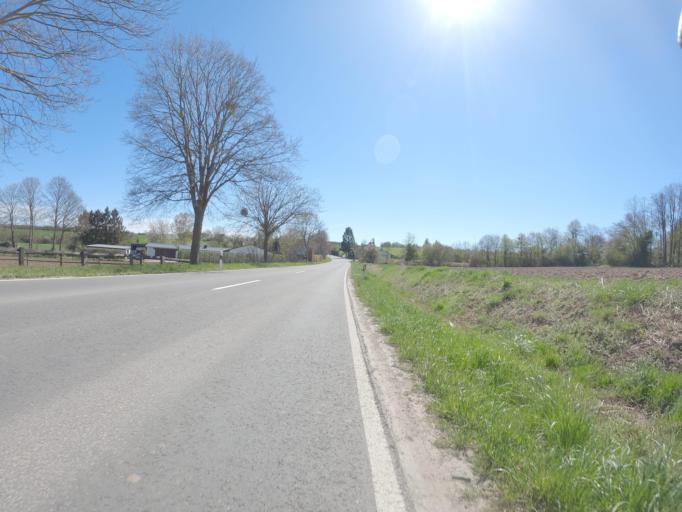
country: DE
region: North Rhine-Westphalia
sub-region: Regierungsbezirk Koln
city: Eschweiler
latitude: 50.7796
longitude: 6.2975
